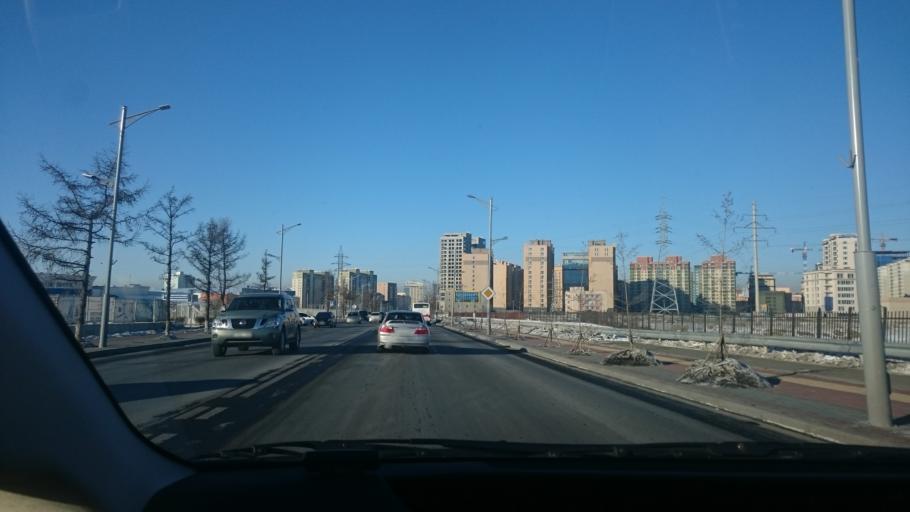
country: MN
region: Ulaanbaatar
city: Ulaanbaatar
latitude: 47.8972
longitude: 106.9331
